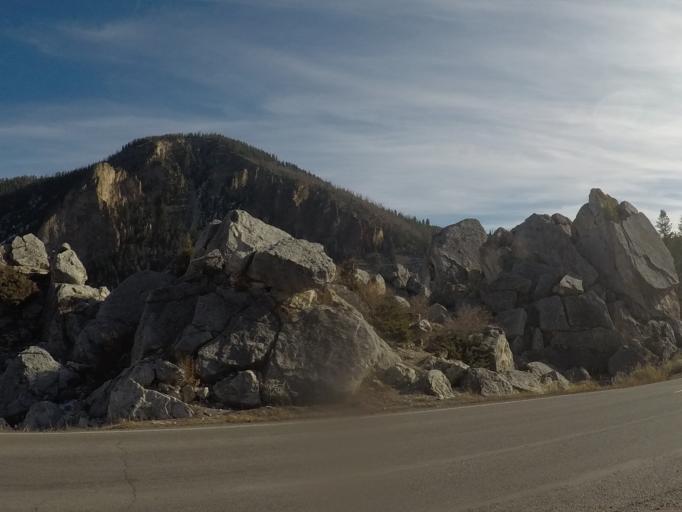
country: US
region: Montana
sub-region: Gallatin County
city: West Yellowstone
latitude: 44.9437
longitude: -110.7174
